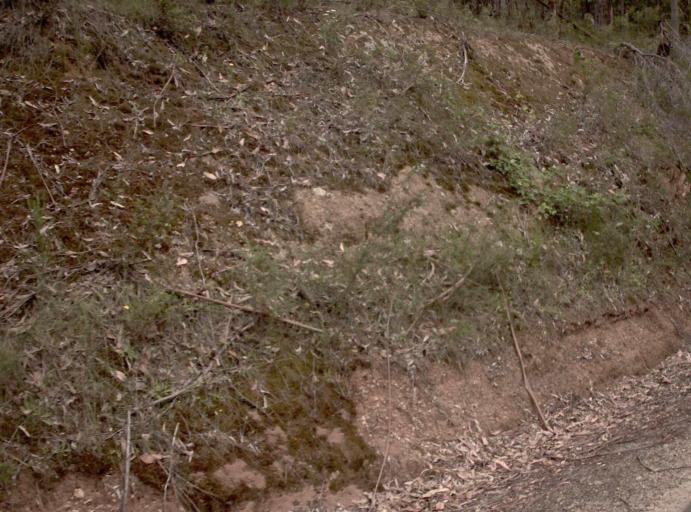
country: AU
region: New South Wales
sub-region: Bombala
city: Bombala
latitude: -37.4075
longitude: 149.1992
